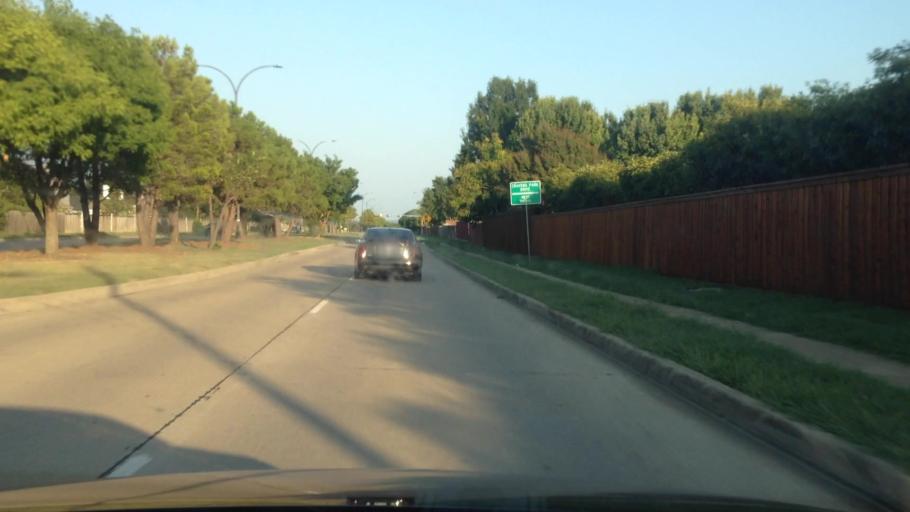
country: US
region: Texas
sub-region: Tarrant County
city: Dalworthington Gardens
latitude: 32.6557
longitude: -97.1024
